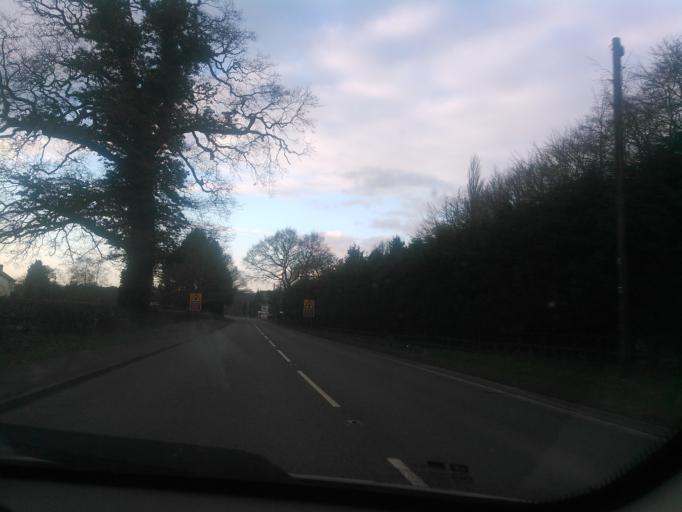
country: GB
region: England
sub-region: Shropshire
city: Stoke upon Tern
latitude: 52.8446
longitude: -2.4697
